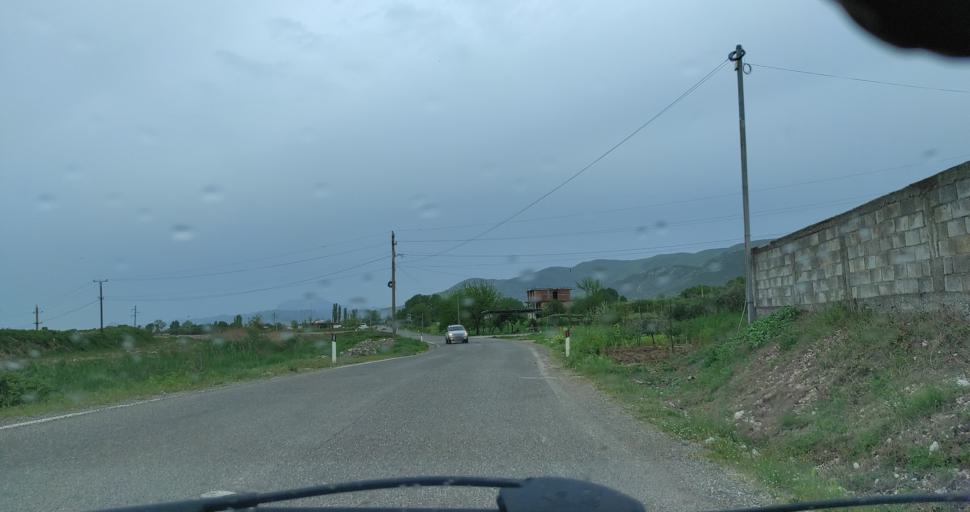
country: AL
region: Lezhe
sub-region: Rrethi i Kurbinit
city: Mamurras
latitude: 41.5954
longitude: 19.6986
